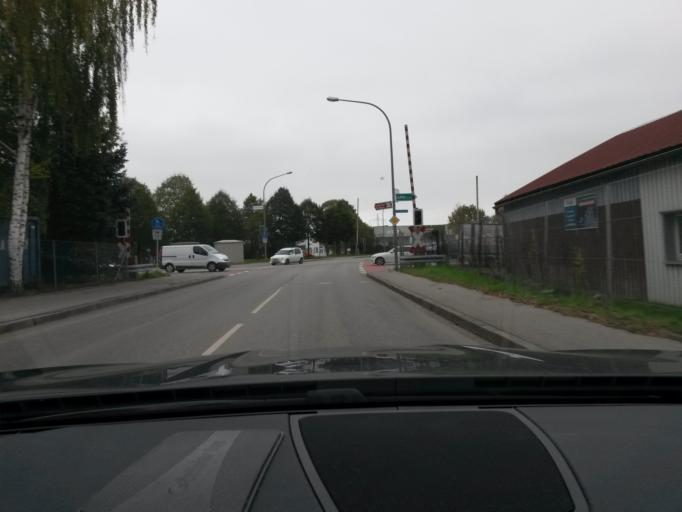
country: DE
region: Bavaria
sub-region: Lower Bavaria
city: Tiefenbach
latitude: 48.5482
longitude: 12.1072
